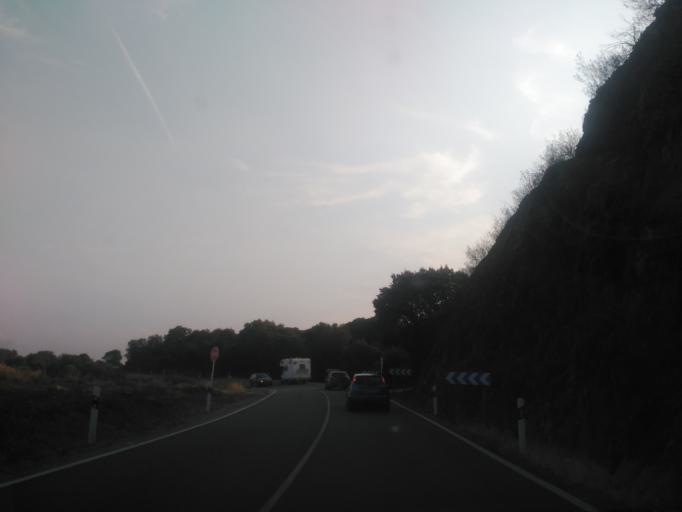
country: ES
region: Castille and Leon
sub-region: Provincia de Zamora
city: Montamarta
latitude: 41.7028
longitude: -5.8147
